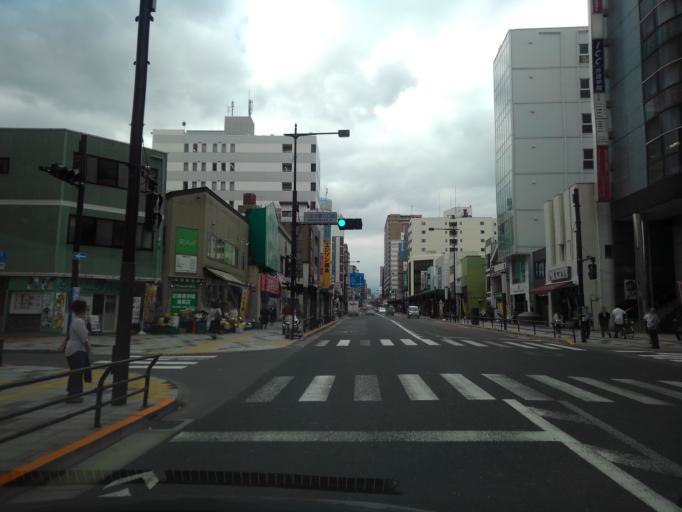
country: JP
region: Tokyo
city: Hachioji
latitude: 35.6597
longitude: 139.3386
